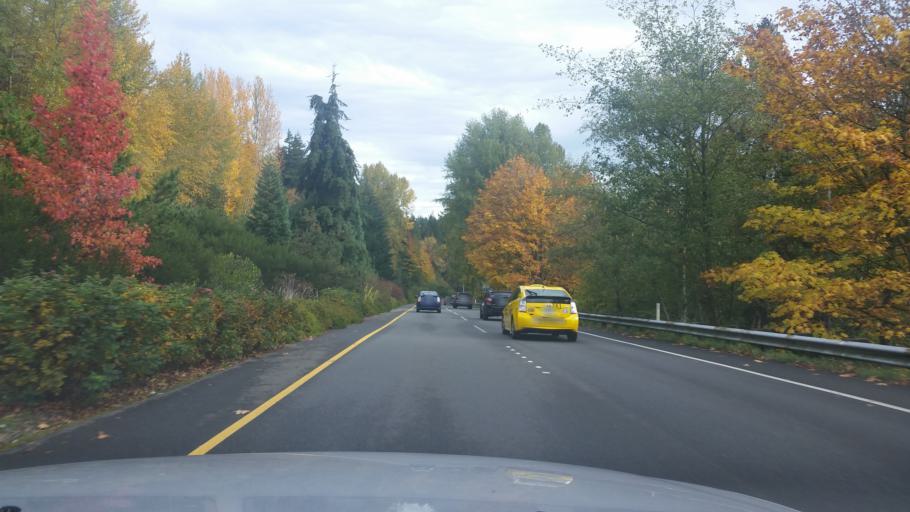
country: US
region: Washington
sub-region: King County
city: Bellevue
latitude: 47.6045
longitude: -122.1816
